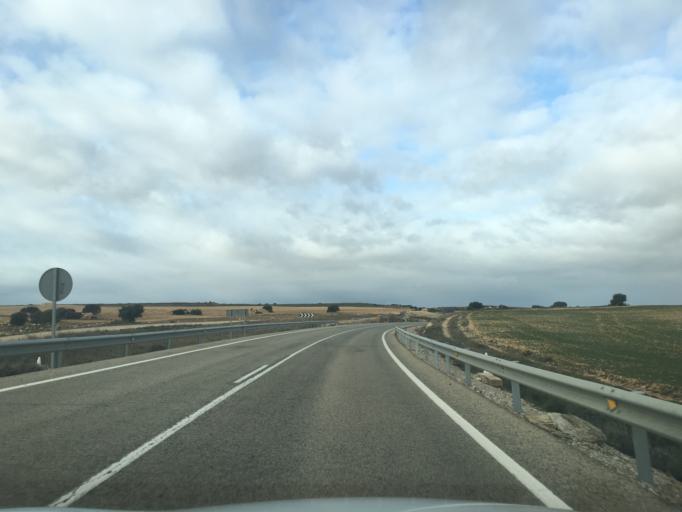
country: ES
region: Castille-La Mancha
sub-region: Provincia de Albacete
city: Petrola
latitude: 38.8238
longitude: -1.5853
